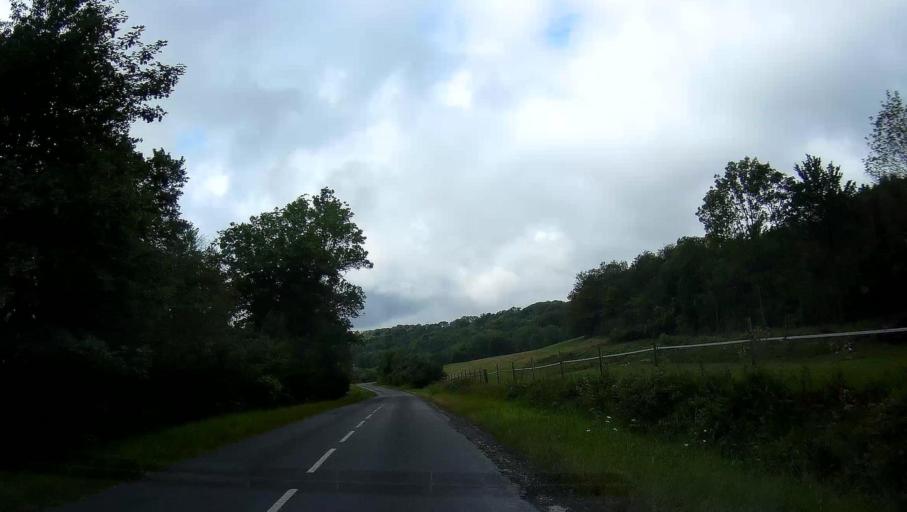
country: FR
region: Picardie
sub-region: Departement de l'Aisne
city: Rozoy-sur-Serre
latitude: 49.6731
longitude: 4.2489
